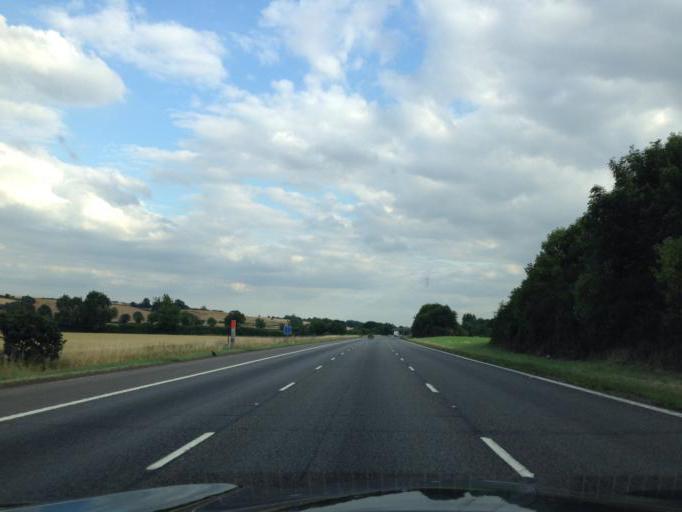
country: GB
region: England
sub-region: Oxfordshire
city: Hanwell
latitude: 52.1134
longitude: -1.3669
